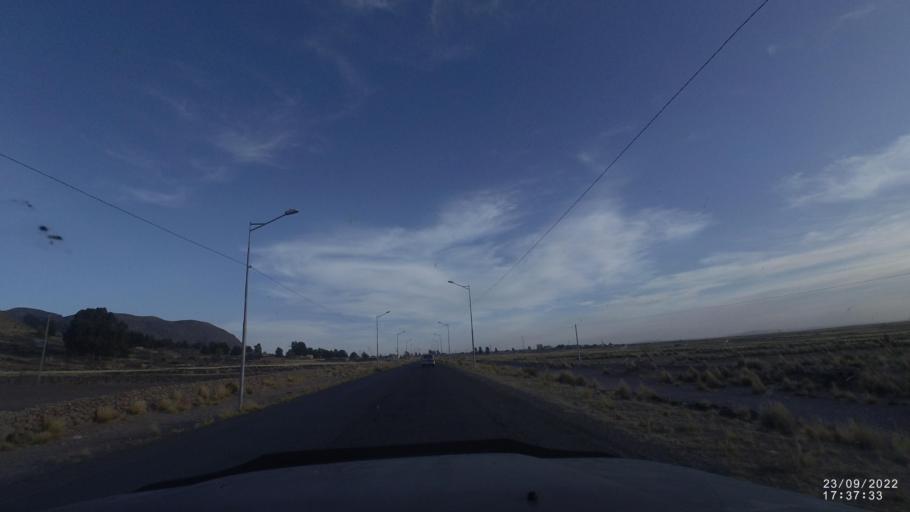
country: BO
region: Oruro
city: Challapata
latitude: -18.9972
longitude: -66.7777
